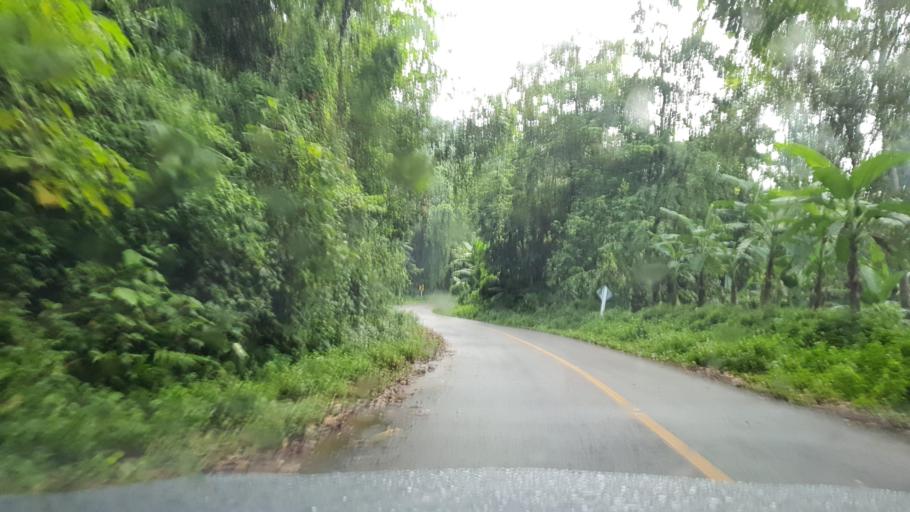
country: TH
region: Chiang Mai
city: Mae On
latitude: 18.9986
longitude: 99.3345
